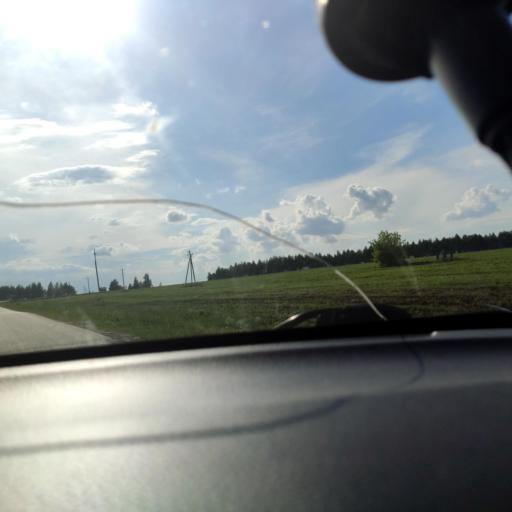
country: RU
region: Tatarstan
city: Verkhniy Uslon
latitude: 55.6384
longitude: 48.8799
